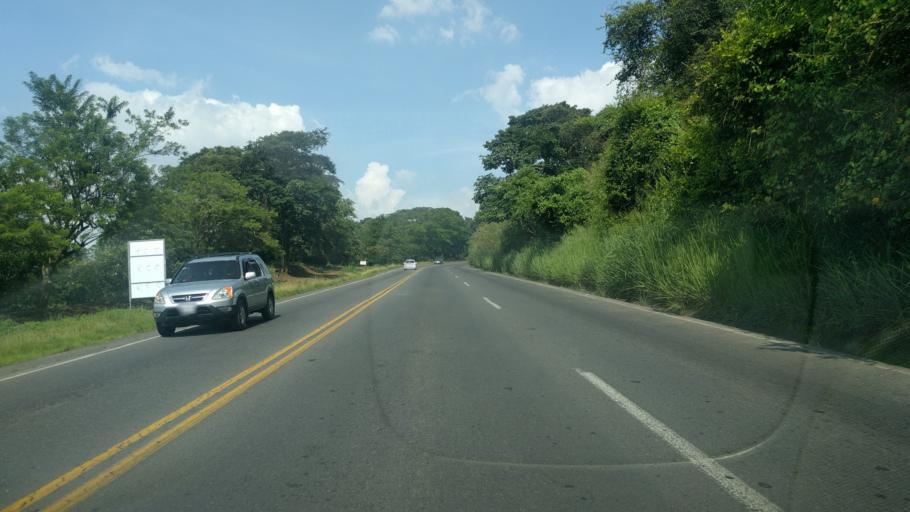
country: CR
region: Alajuela
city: Carrillos
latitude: 10.0179
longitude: -84.3325
